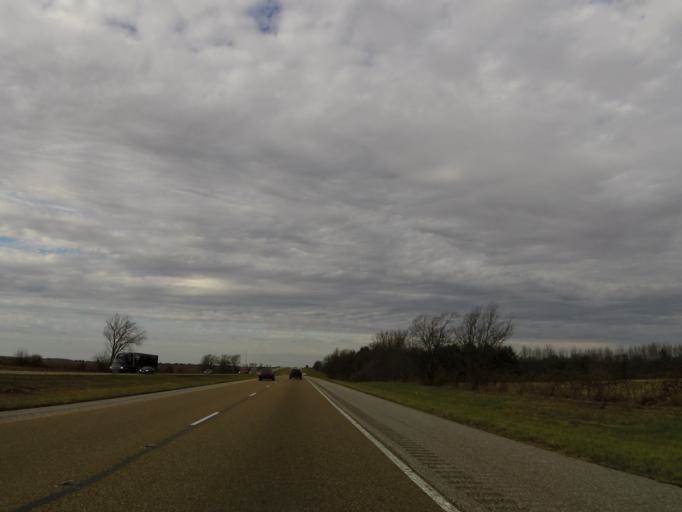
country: US
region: Illinois
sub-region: Clinton County
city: Wamac
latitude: 38.3899
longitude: -89.2297
